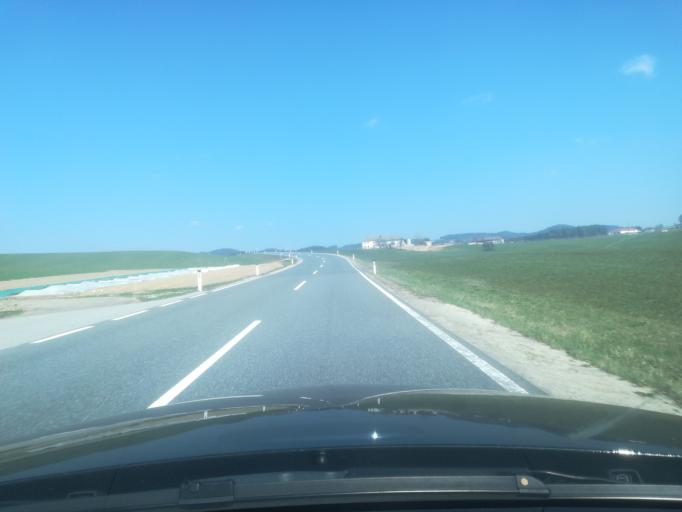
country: AT
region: Upper Austria
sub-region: Politischer Bezirk Perg
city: Perg
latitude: 48.3677
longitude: 14.6820
